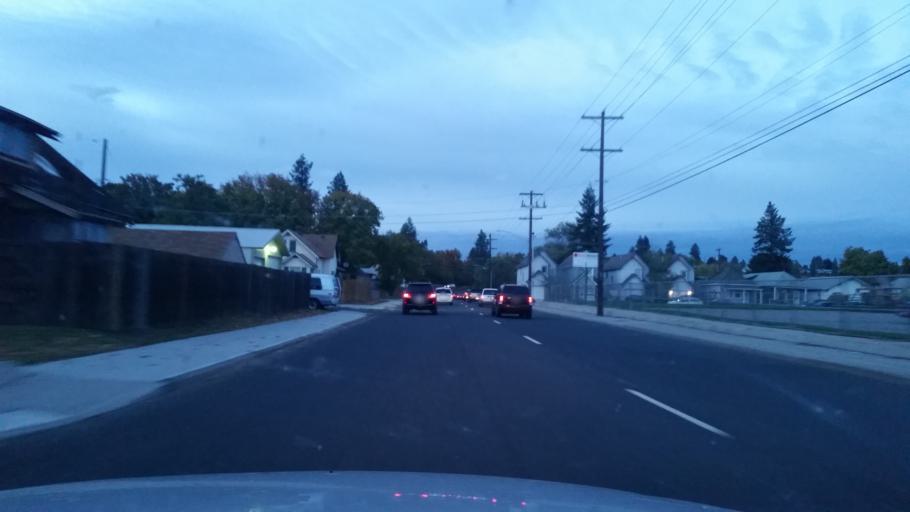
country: US
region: Washington
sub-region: Spokane County
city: Spokane
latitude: 47.6835
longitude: -117.4354
